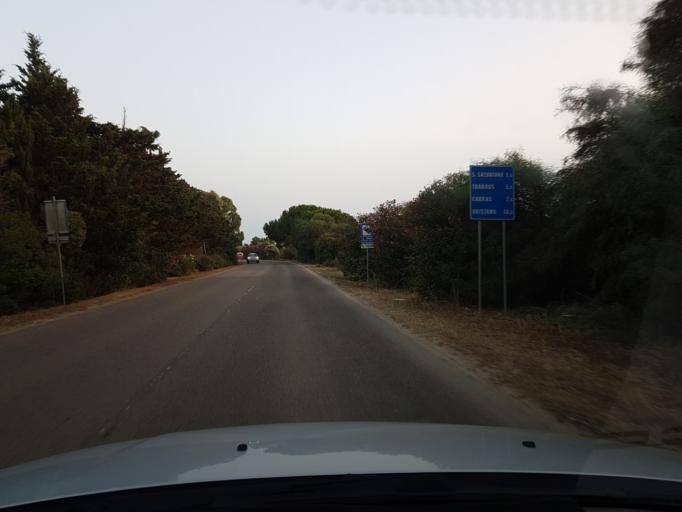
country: IT
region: Sardinia
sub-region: Provincia di Oristano
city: Cabras
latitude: 39.9274
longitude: 8.4550
